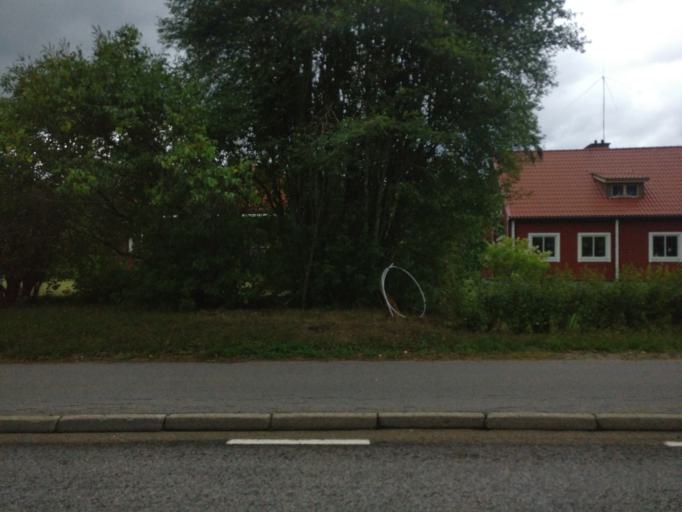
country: SE
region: Vaermland
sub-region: Torsby Kommun
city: Torsby
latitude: 60.7256
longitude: 12.8767
